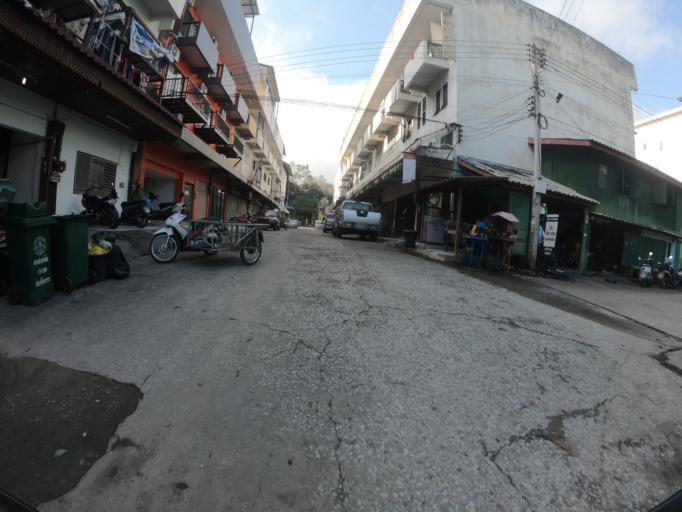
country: TH
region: Chiang Mai
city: Chiang Mai
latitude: 18.8093
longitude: 98.9548
